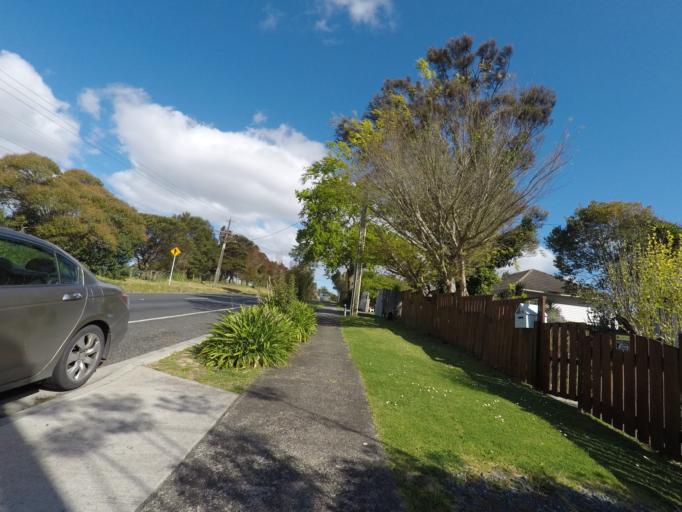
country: NZ
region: Auckland
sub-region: Auckland
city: Rosebank
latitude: -36.8554
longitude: 174.6035
